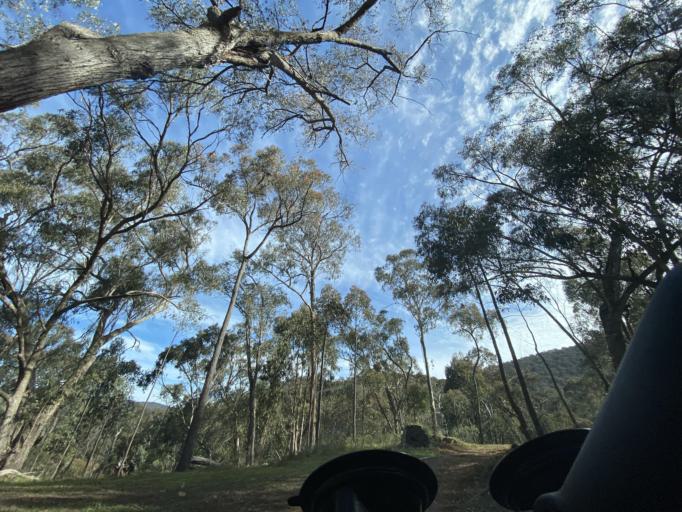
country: AU
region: Victoria
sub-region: Mansfield
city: Mansfield
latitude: -36.8113
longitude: 146.1161
